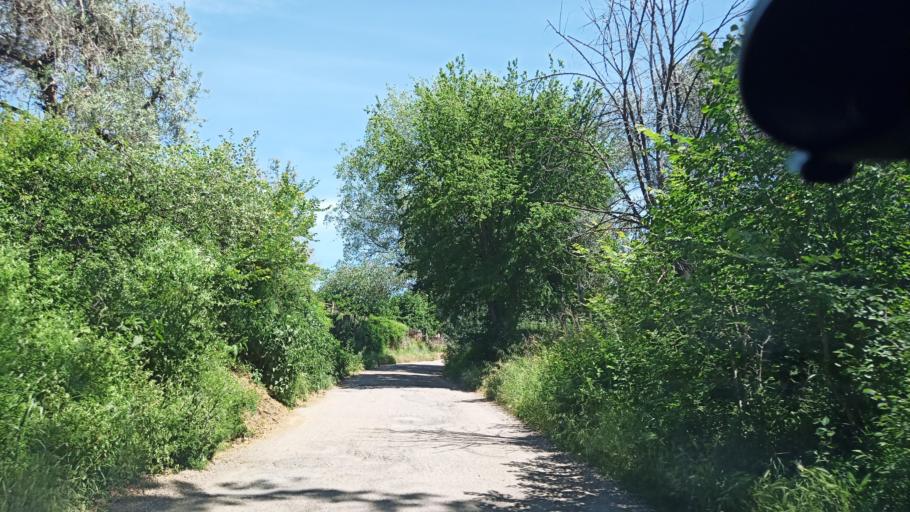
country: IT
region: Latium
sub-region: Provincia di Rieti
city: Torri in Sabina
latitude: 42.3470
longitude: 12.6186
